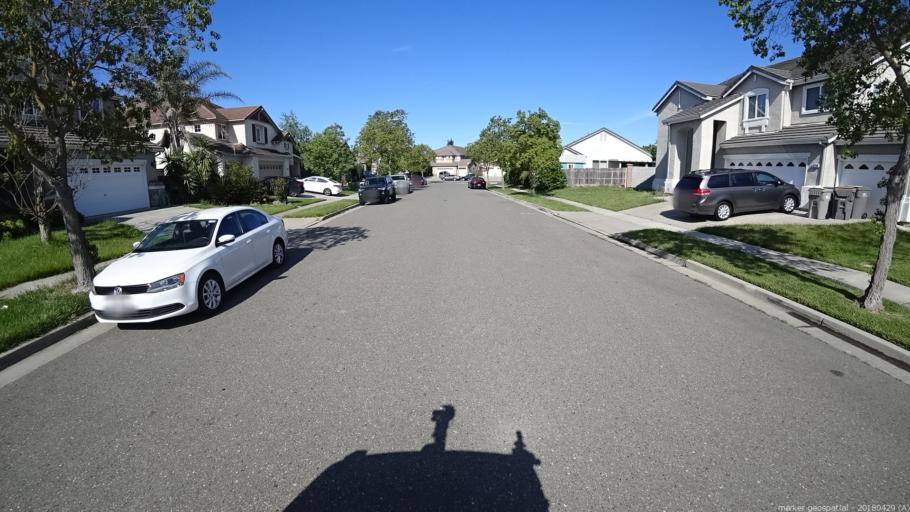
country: US
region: California
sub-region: Yolo County
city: West Sacramento
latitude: 38.5378
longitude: -121.5773
